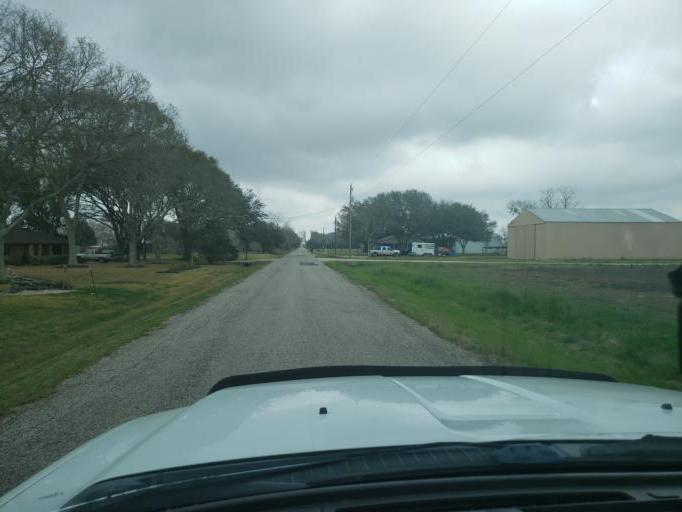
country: US
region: Texas
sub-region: Fort Bend County
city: Needville
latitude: 29.3418
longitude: -95.7629
